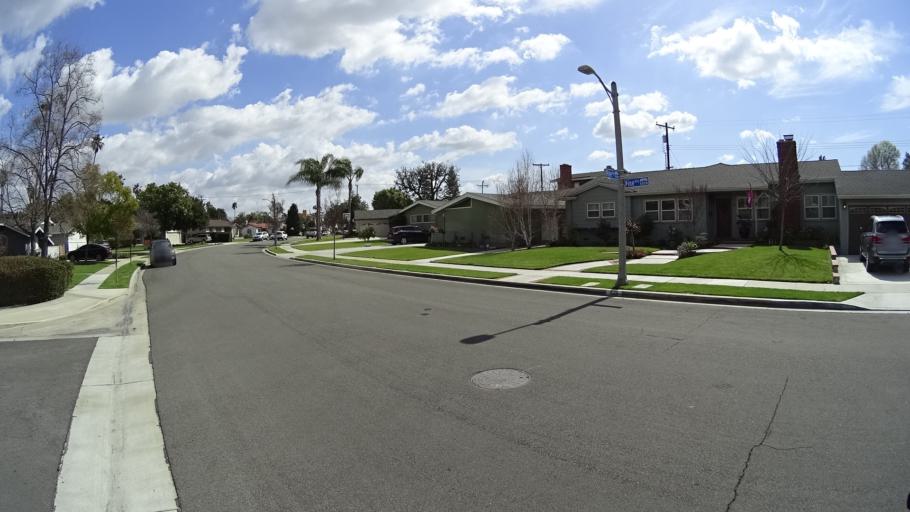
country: US
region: California
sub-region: Orange County
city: Anaheim
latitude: 33.8392
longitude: -117.9225
